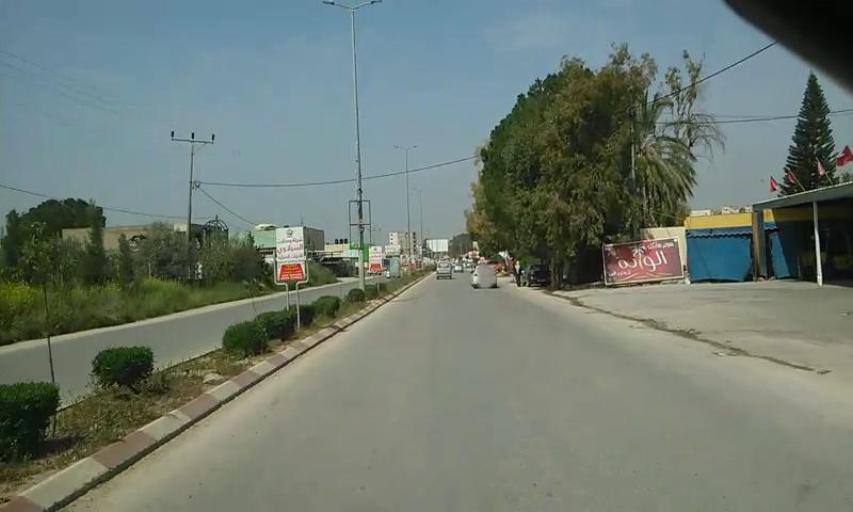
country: PS
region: West Bank
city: Janin
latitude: 32.4749
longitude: 35.3015
